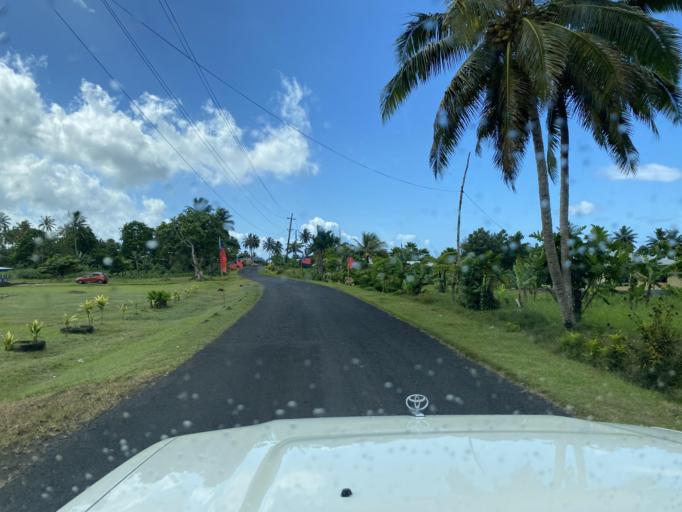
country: WS
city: Matavai
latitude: -13.9886
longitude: -171.5870
